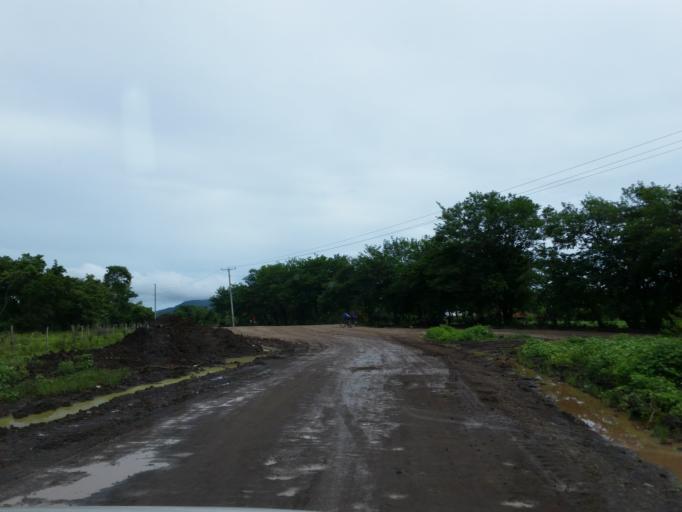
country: NI
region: Leon
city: Larreynaga
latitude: 12.5779
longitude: -86.6231
